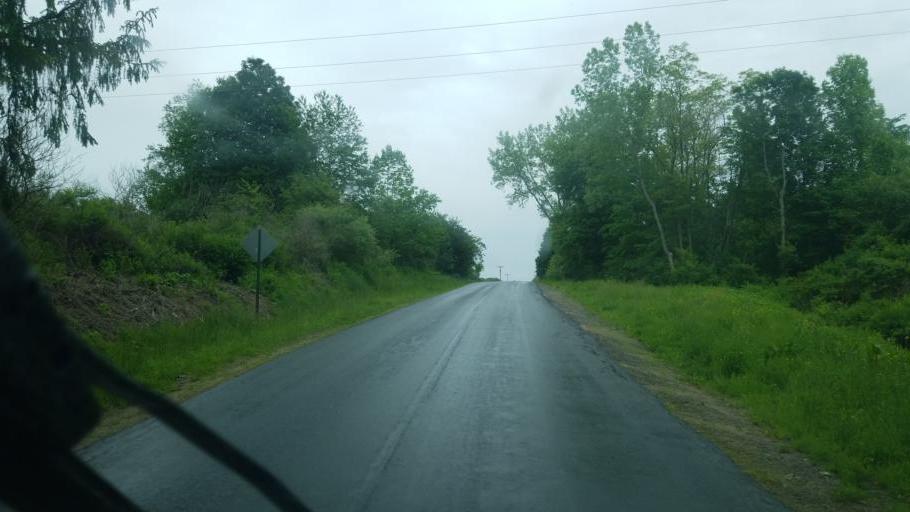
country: US
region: New York
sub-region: Herkimer County
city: Frankfort
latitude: 43.0656
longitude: -75.0547
